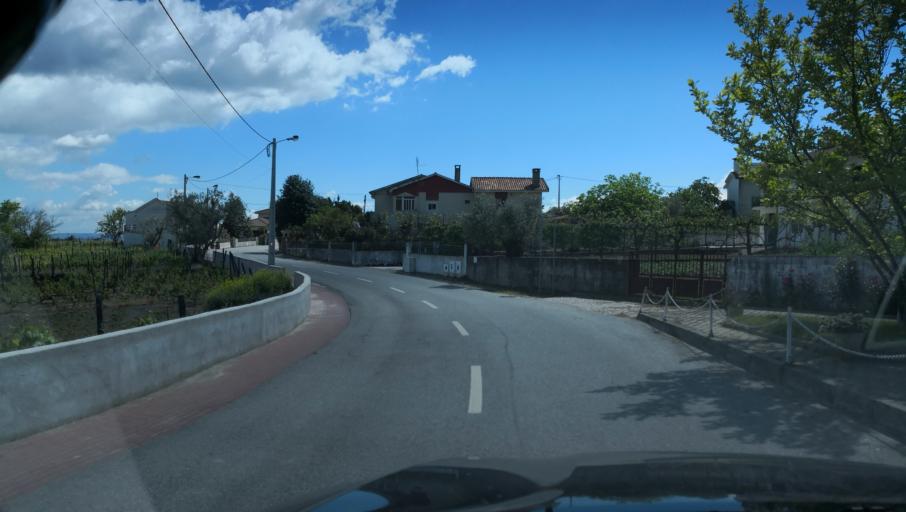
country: PT
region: Vila Real
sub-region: Vila Real
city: Vila Real
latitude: 41.2603
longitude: -7.7325
